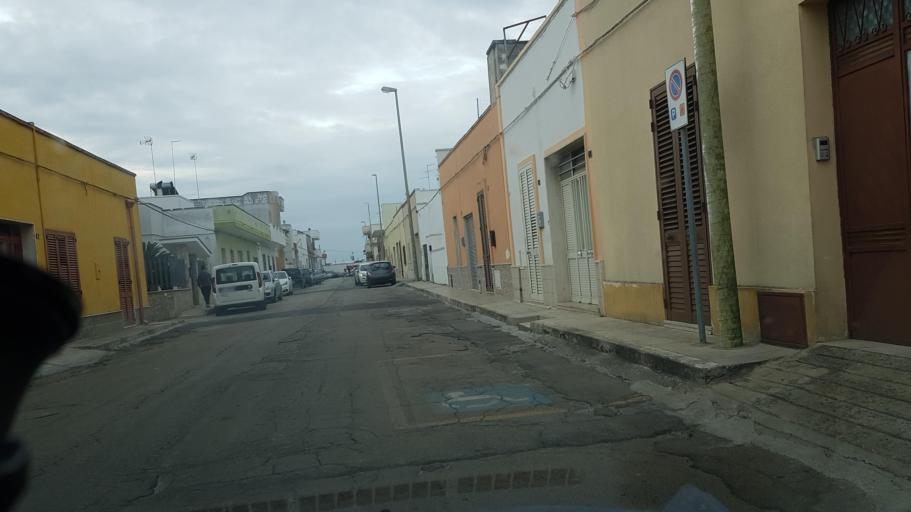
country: IT
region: Apulia
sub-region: Provincia di Lecce
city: Veglie
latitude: 40.3351
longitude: 17.9602
